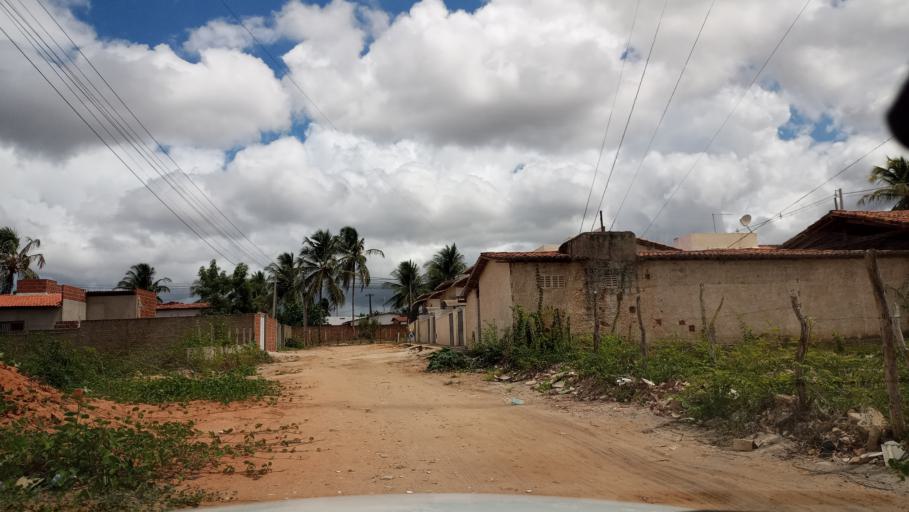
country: BR
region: Rio Grande do Norte
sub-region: Joao Camara
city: Joao Camara
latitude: -5.5361
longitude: -35.8106
